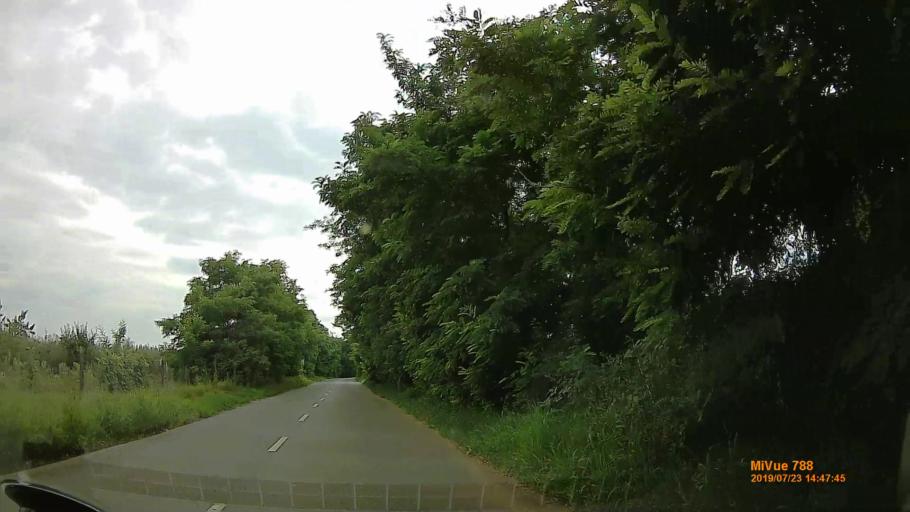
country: HU
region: Szabolcs-Szatmar-Bereg
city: Nyiregyhaza
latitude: 47.9090
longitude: 21.6735
